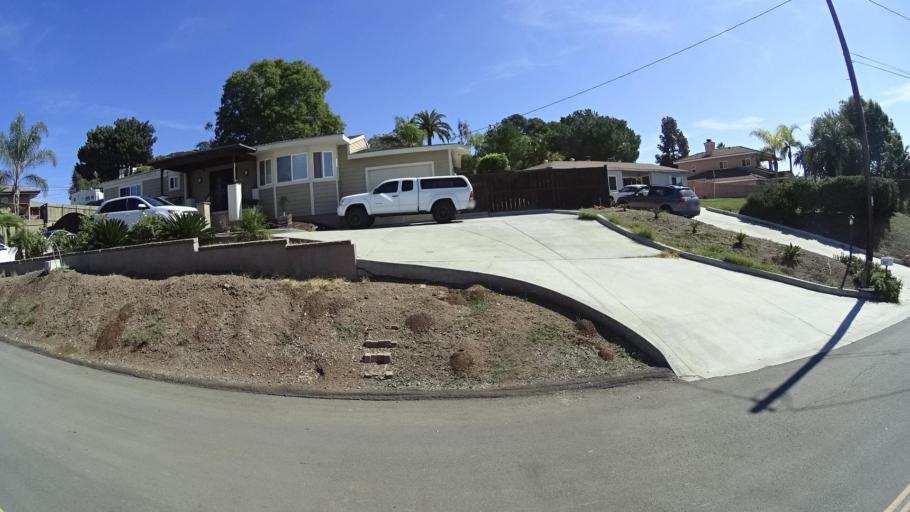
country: US
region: California
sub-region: San Diego County
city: Casa de Oro-Mount Helix
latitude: 32.7489
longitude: -116.9698
